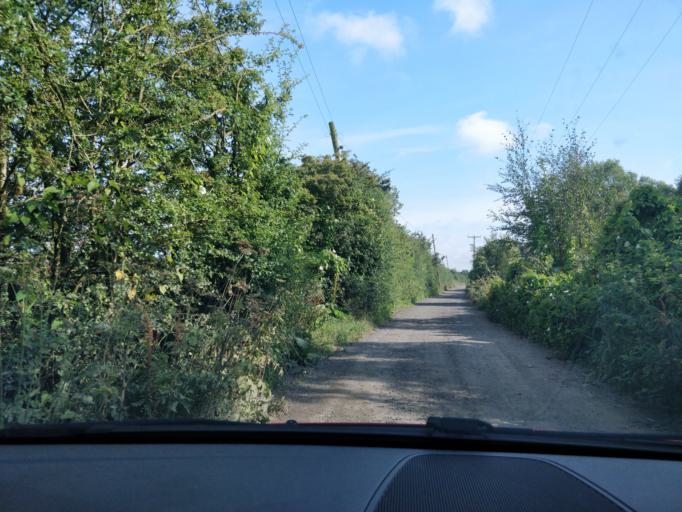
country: GB
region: England
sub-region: Sefton
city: Southport
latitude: 53.6512
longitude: -2.9561
